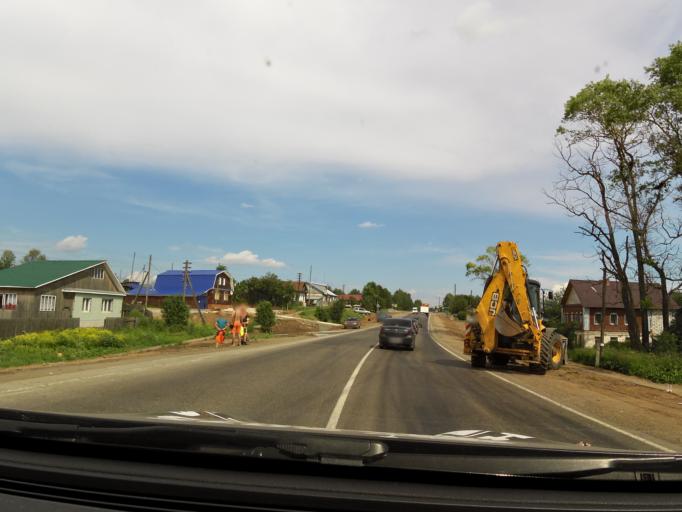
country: RU
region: Kirov
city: Vakhrushi
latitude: 58.6773
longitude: 49.9716
